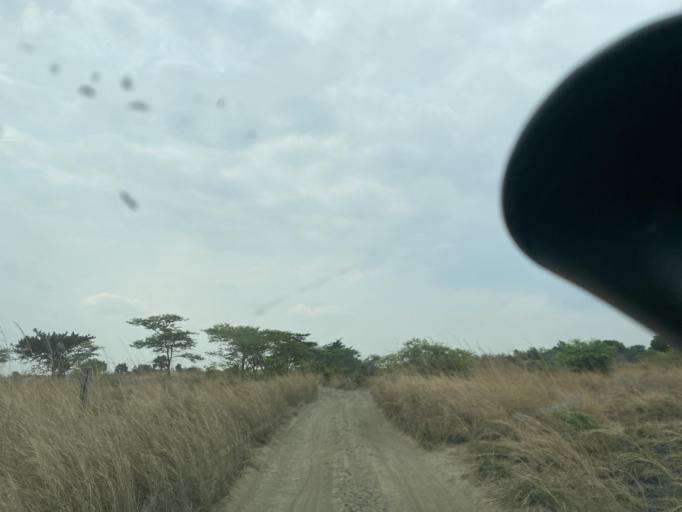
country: ZM
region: Lusaka
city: Lusaka
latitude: -15.2454
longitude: 28.3326
